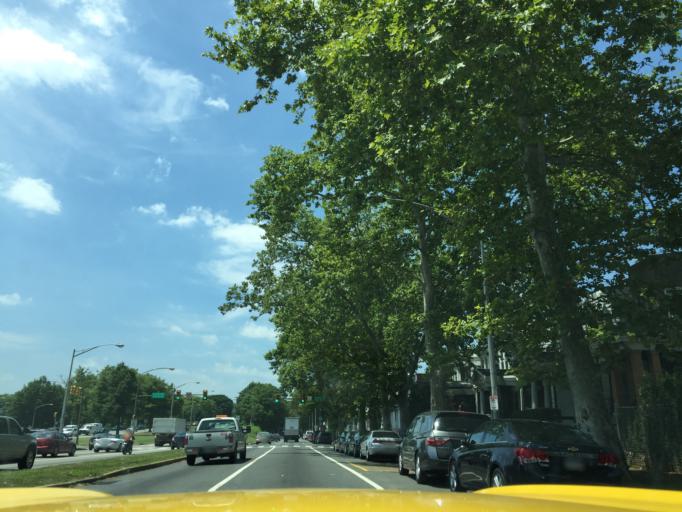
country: US
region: Pennsylvania
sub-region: Montgomery County
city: Rockledge
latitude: 40.0249
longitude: -75.1296
